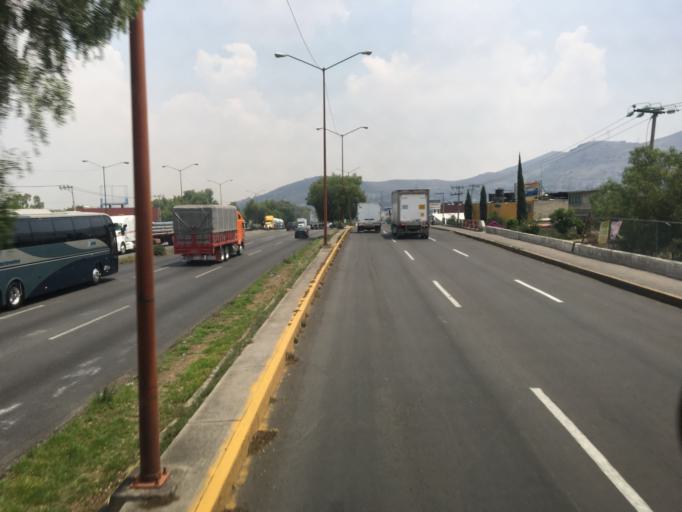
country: MX
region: Mexico
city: Tlalnepantla
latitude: 19.5457
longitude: -99.1829
